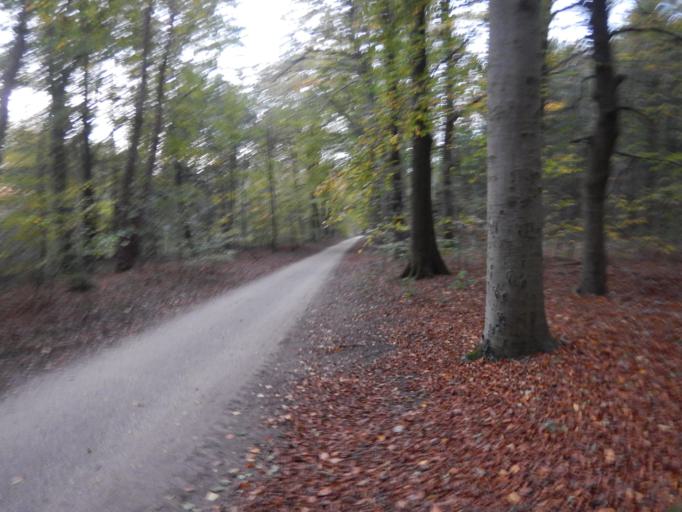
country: NL
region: Gelderland
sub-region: Gemeente Putten
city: Putten
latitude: 52.2516
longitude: 5.6326
